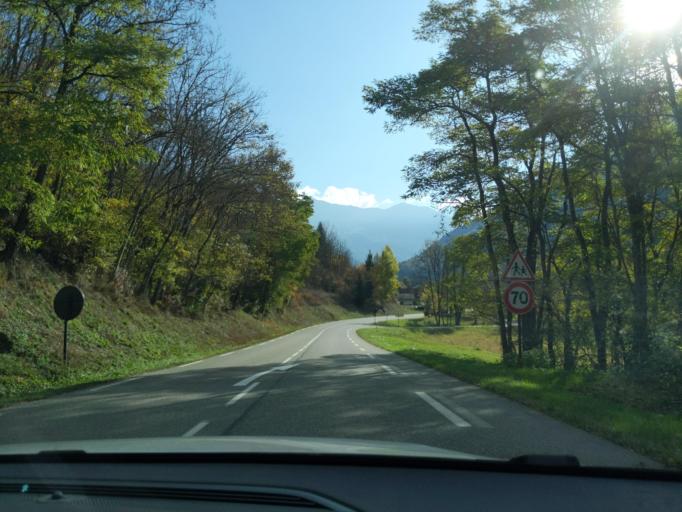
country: FR
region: Rhone-Alpes
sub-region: Departement de la Savoie
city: Seez
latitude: 45.6157
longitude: 6.8205
